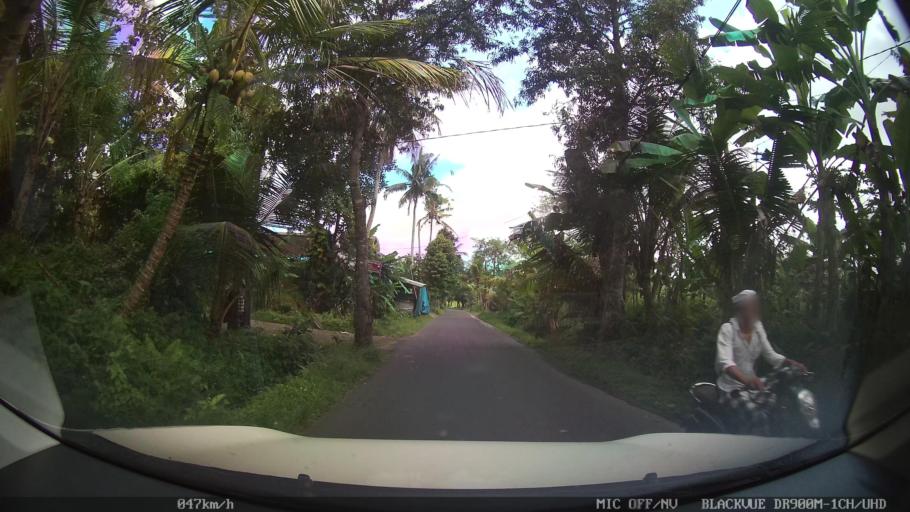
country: ID
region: Bali
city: Banjar Madangan Kaja
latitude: -8.4881
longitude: 115.3208
